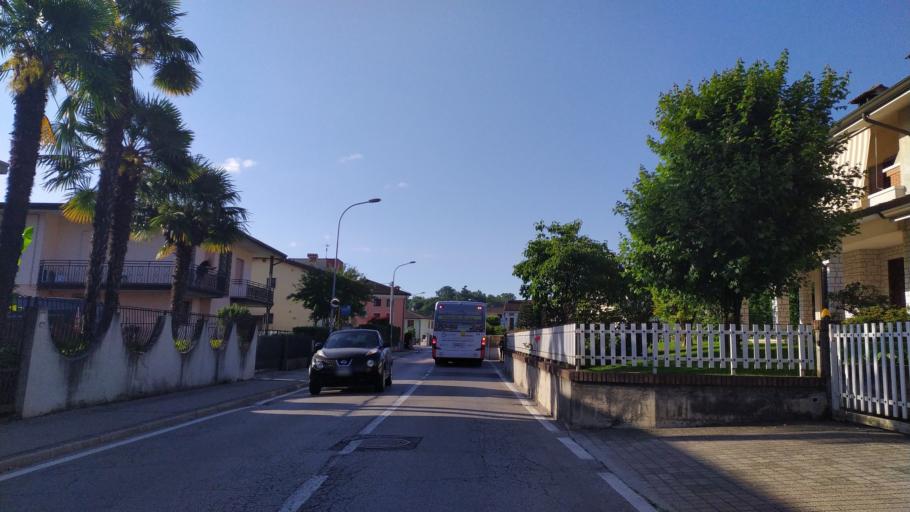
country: IT
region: Veneto
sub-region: Provincia di Vicenza
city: Isola Vicentina
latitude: 45.6230
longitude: 11.4498
